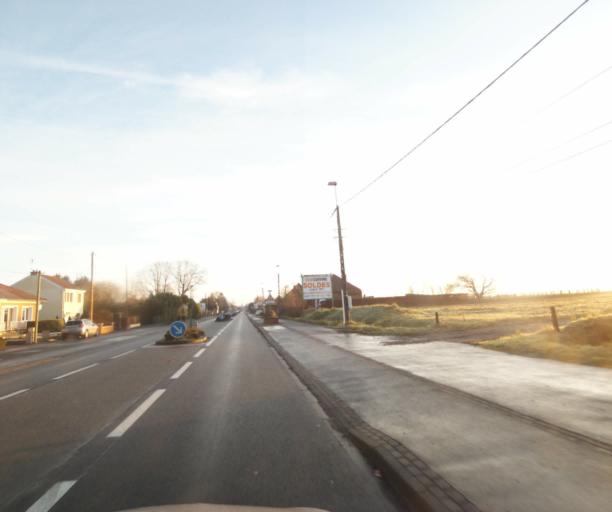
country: FR
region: Nord-Pas-de-Calais
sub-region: Departement du Nord
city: Saint-Saulve
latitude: 50.3777
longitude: 3.5749
